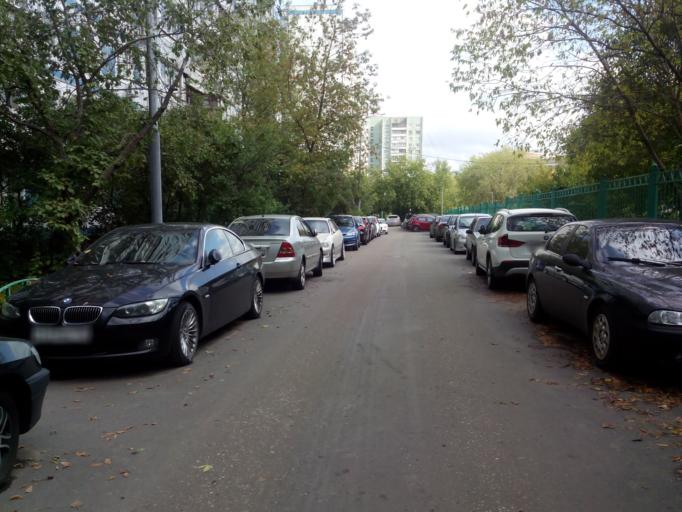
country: RU
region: Moscow
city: Ostankinskiy
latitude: 55.8253
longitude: 37.6238
